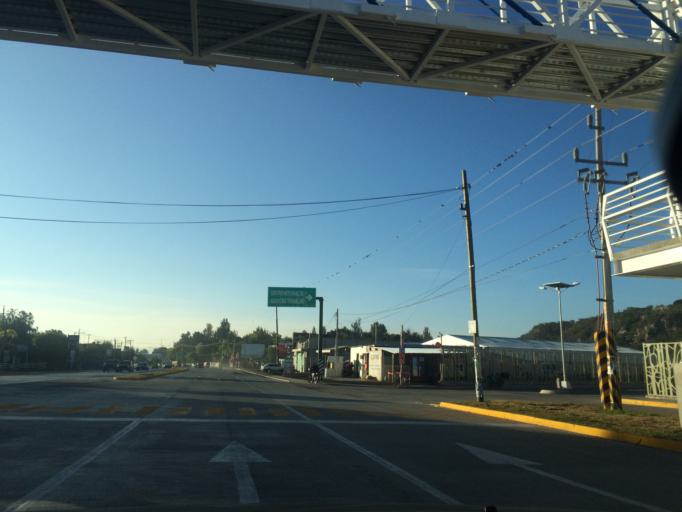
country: MX
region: Puebla
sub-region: Santiago Miahuatlan
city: San Jose Monte Chiquito
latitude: 18.4769
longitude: -97.4385
